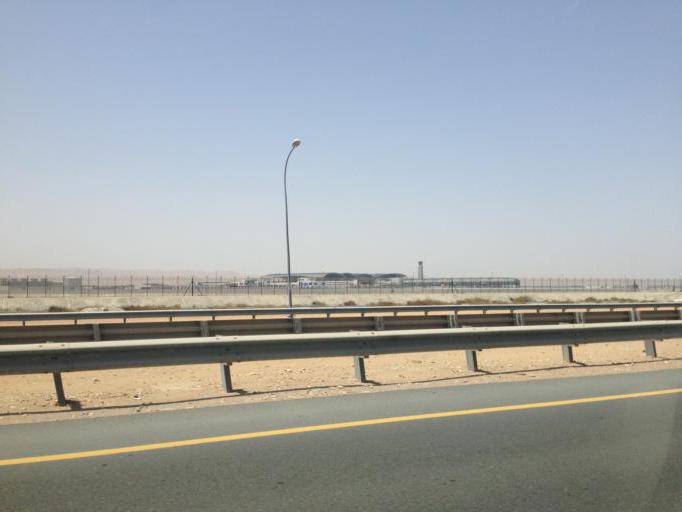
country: OM
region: Muhafazat Masqat
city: Bawshar
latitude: 23.6116
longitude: 58.3008
